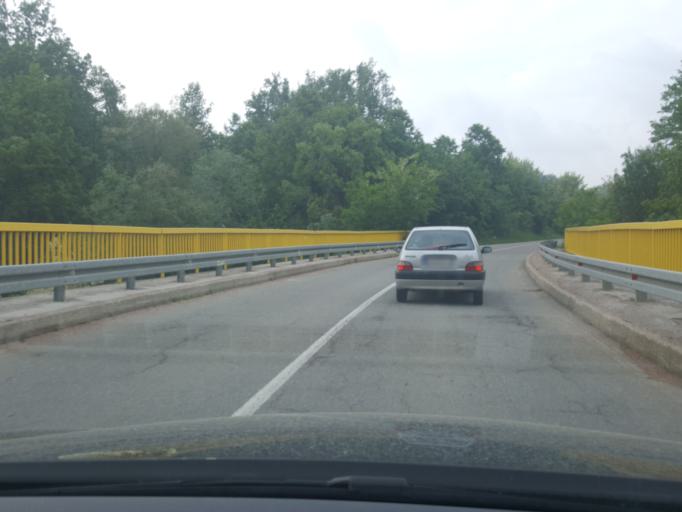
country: RS
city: Kamenica
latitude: 44.2115
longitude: 19.7149
